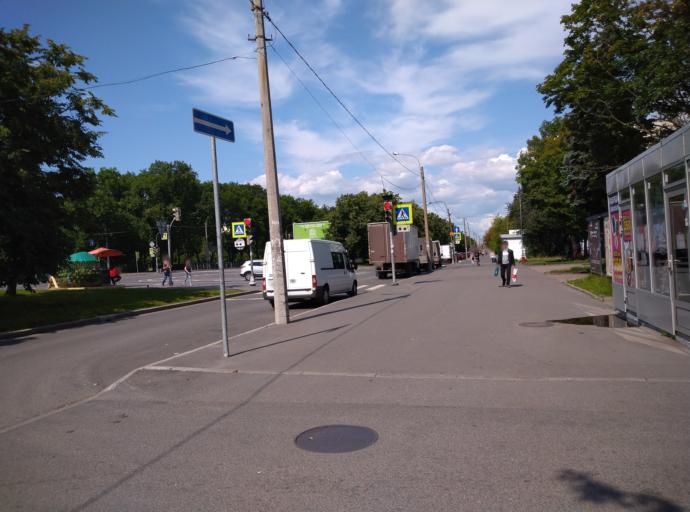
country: RU
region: St.-Petersburg
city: Kupchino
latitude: 59.8579
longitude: 30.3380
